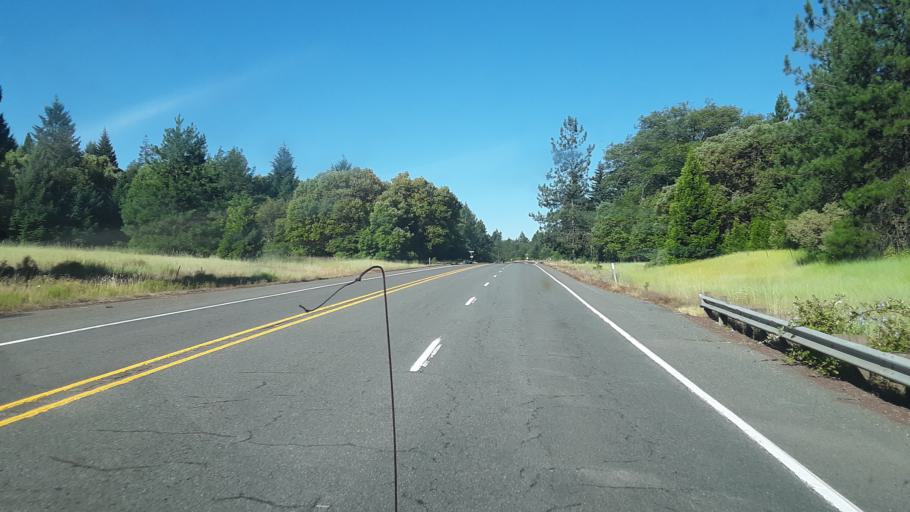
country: US
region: Oregon
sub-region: Jackson County
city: Shady Cove
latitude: 42.6890
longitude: -122.6025
